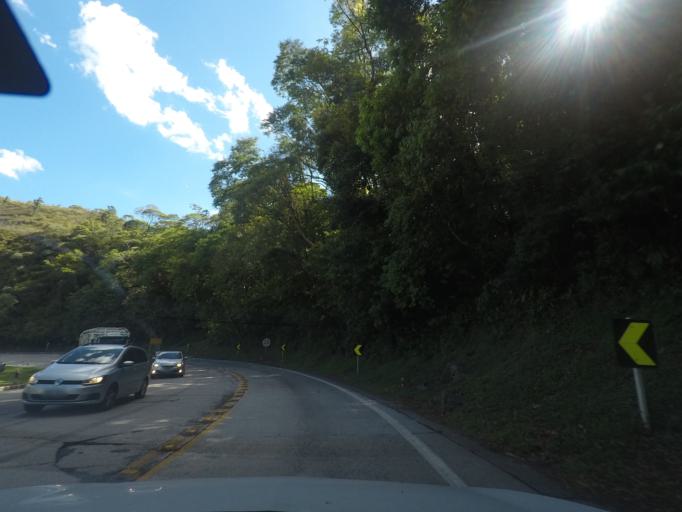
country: BR
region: Rio de Janeiro
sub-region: Guapimirim
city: Guapimirim
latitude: -22.4826
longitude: -42.9972
